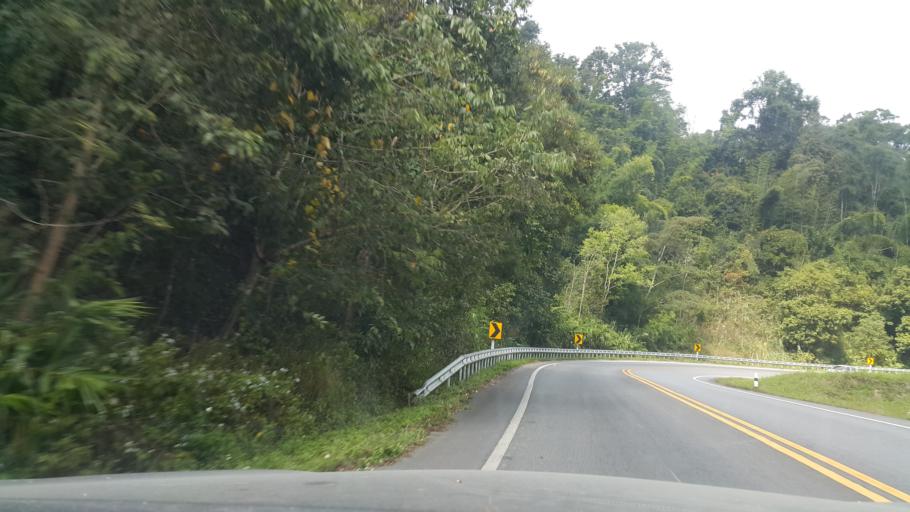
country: TH
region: Lampang
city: Wang Nuea
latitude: 19.0667
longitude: 99.7593
